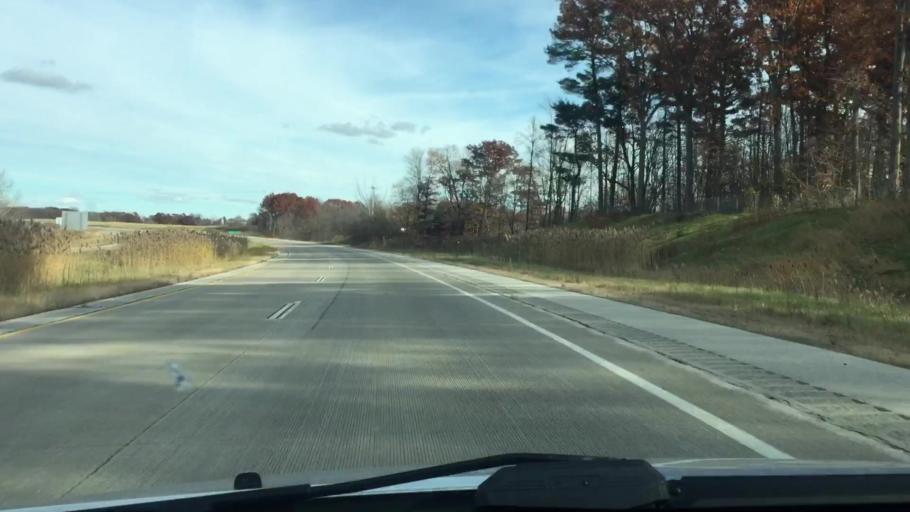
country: US
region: Wisconsin
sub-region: Kewaunee County
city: Luxemburg
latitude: 44.6336
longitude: -87.7652
